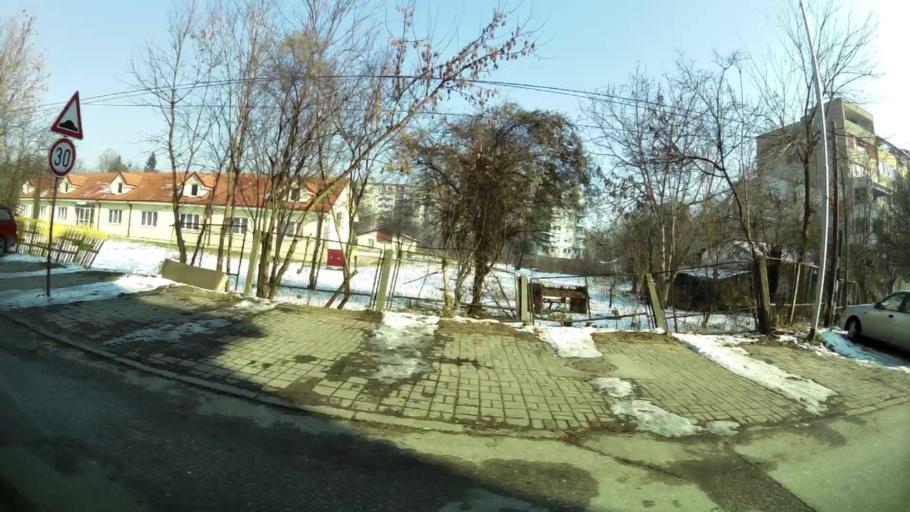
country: MK
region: Kisela Voda
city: Usje
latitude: 41.9745
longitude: 21.4409
